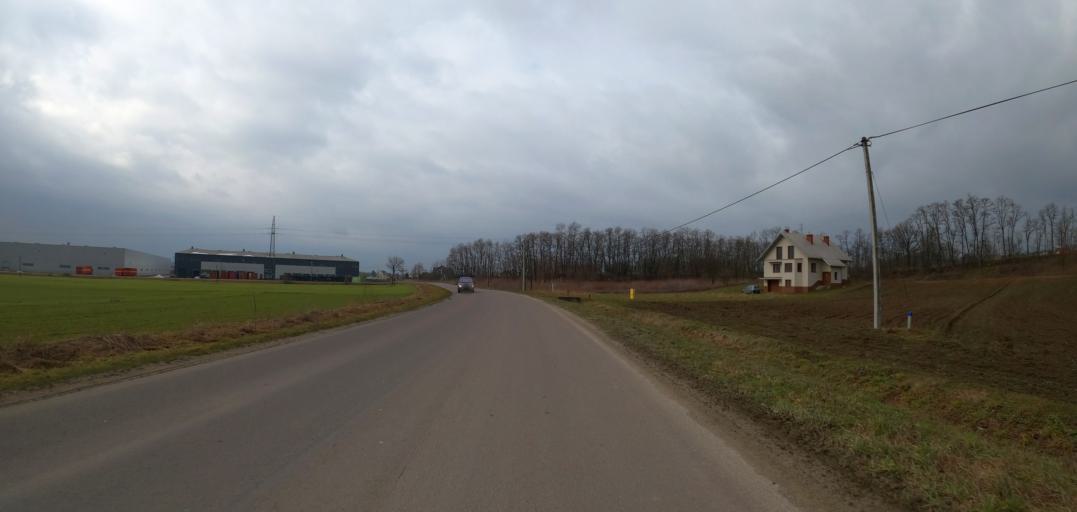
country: PL
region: Subcarpathian Voivodeship
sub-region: Powiat debicki
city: Pilzno
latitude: 49.9865
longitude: 21.3241
